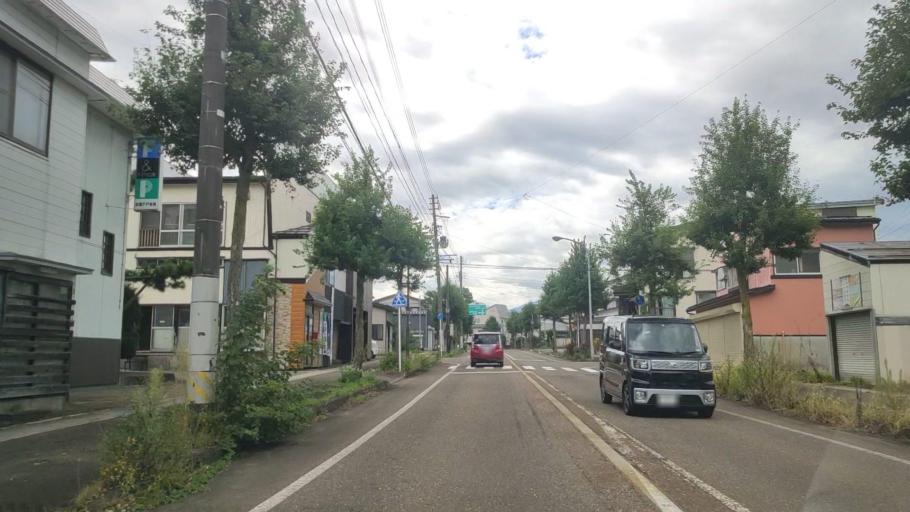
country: JP
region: Niigata
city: Arai
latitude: 37.0271
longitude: 138.2467
